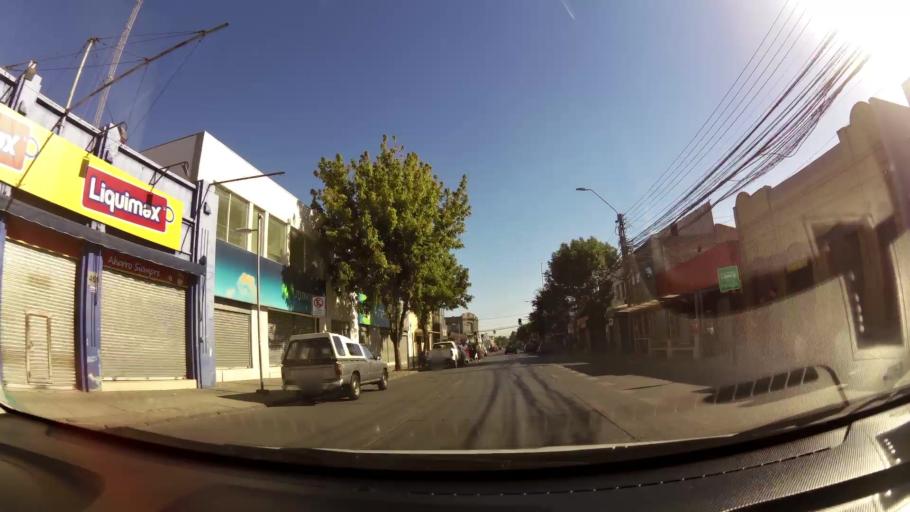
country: CL
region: O'Higgins
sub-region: Provincia de Cachapoal
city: Rancagua
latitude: -34.1704
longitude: -70.7465
